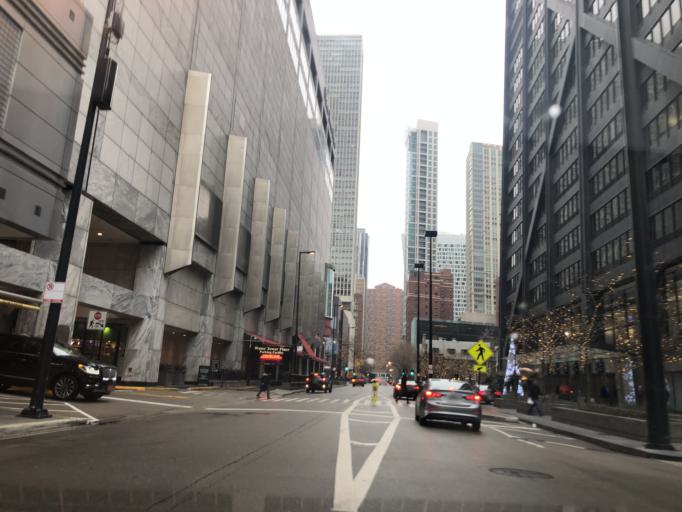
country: US
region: Illinois
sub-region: Cook County
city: Chicago
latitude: 41.8984
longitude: -87.6223
